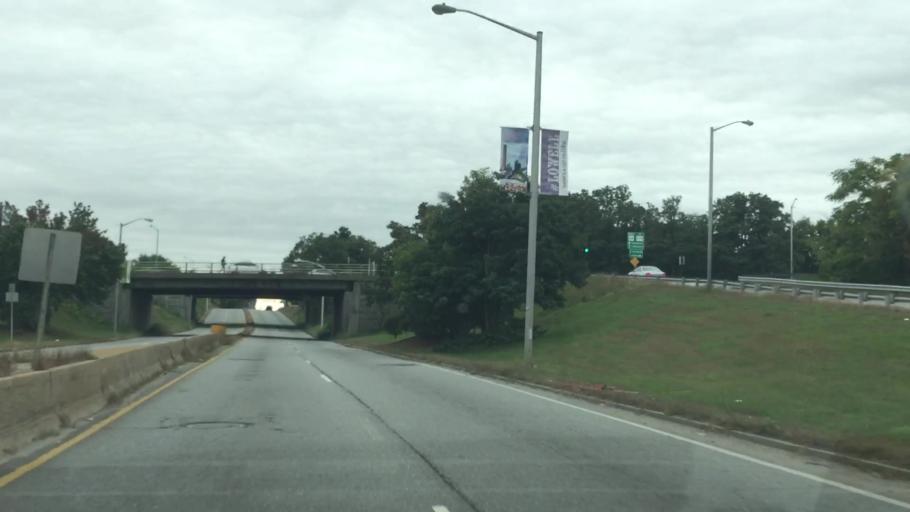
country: US
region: Massachusetts
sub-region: Middlesex County
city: Lowell
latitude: 42.6402
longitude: -71.3165
